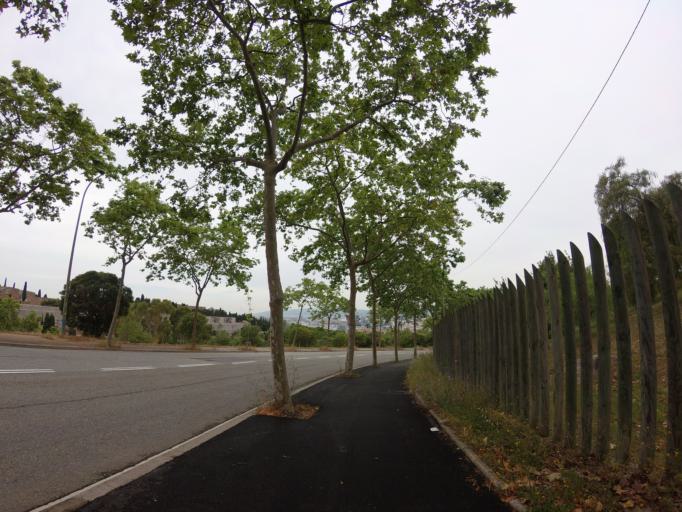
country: ES
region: Catalonia
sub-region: Provincia de Barcelona
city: Sants-Montjuic
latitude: 41.3597
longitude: 2.1575
